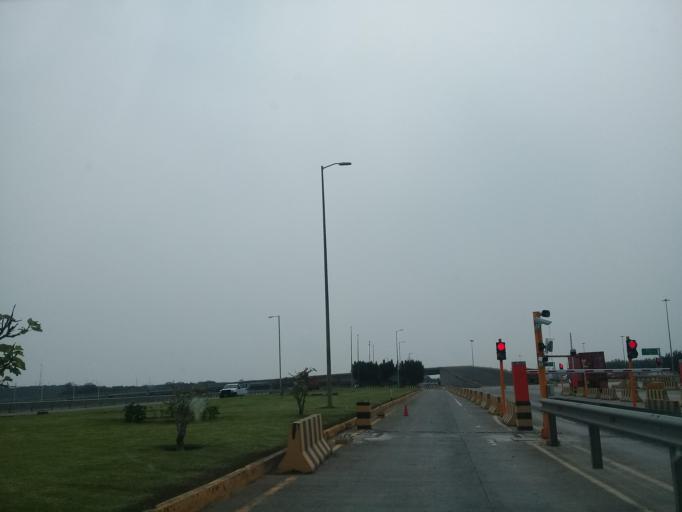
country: MX
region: Veracruz
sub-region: Veracruz
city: Rio Medio [Granja]
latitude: 19.2269
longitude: -96.1858
